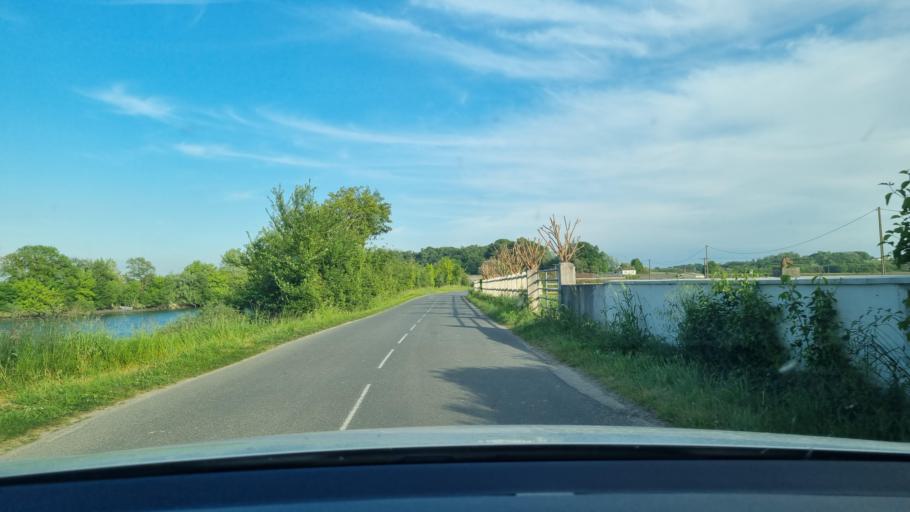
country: FR
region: Aquitaine
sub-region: Departement des Landes
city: Peyrehorade
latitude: 43.5411
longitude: -1.1636
